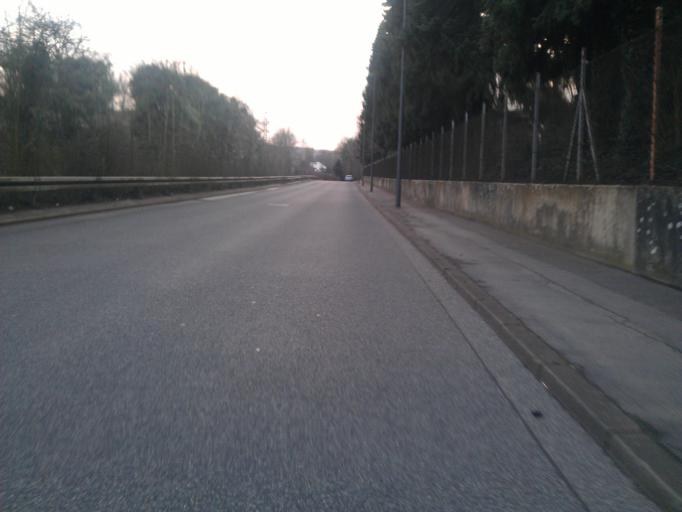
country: DE
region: North Rhine-Westphalia
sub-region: Regierungsbezirk Koln
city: Aachen
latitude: 50.7708
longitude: 6.0554
